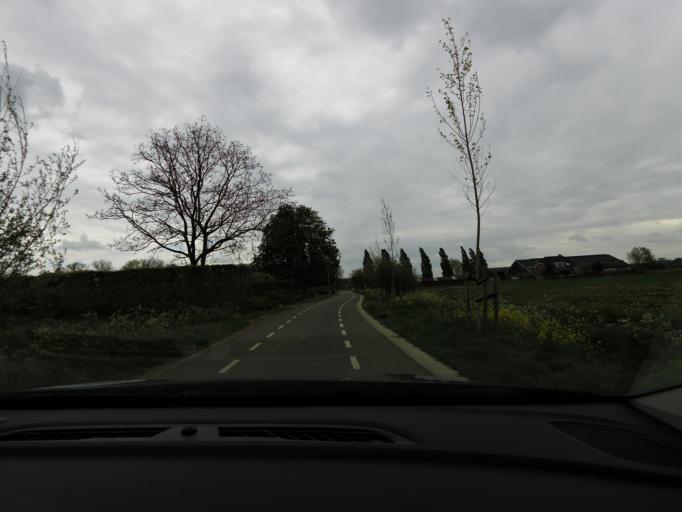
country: NL
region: North Brabant
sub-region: Gemeente Woudrichem
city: Woudrichem
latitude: 51.8567
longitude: 5.0305
